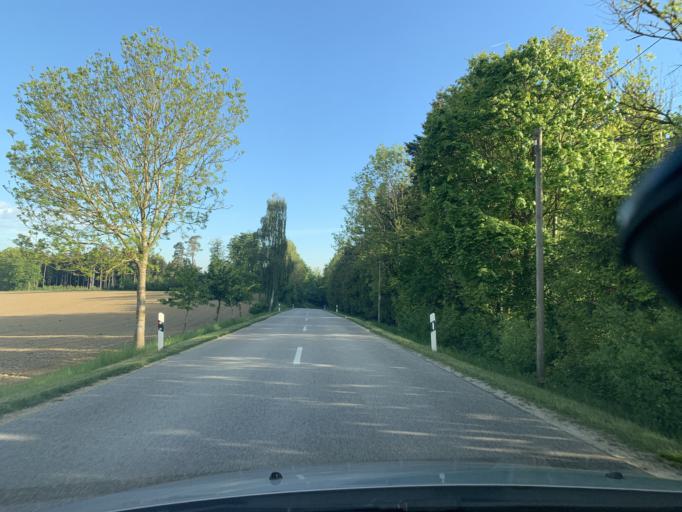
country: DE
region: Bavaria
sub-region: Lower Bavaria
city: Stallwang
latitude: 48.5254
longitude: 12.2315
